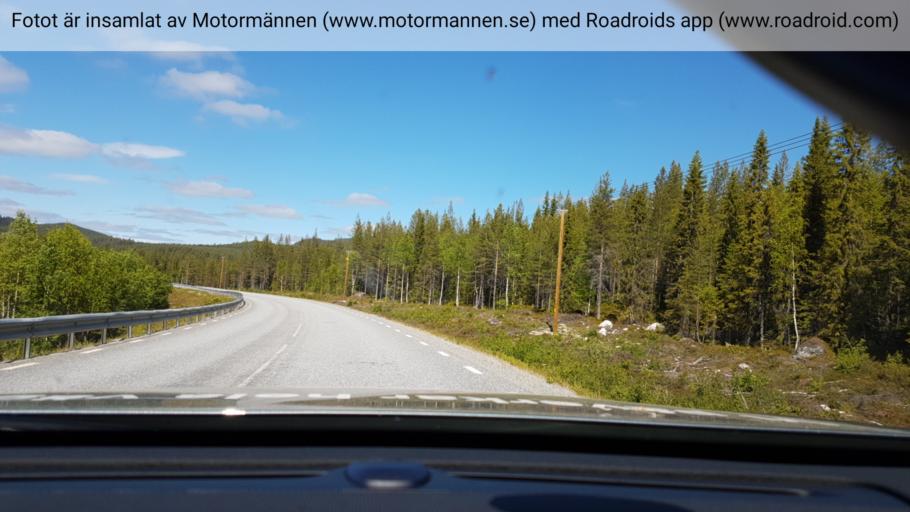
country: SE
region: Vaesterbotten
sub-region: Asele Kommun
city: Asele
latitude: 64.3188
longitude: 17.2106
